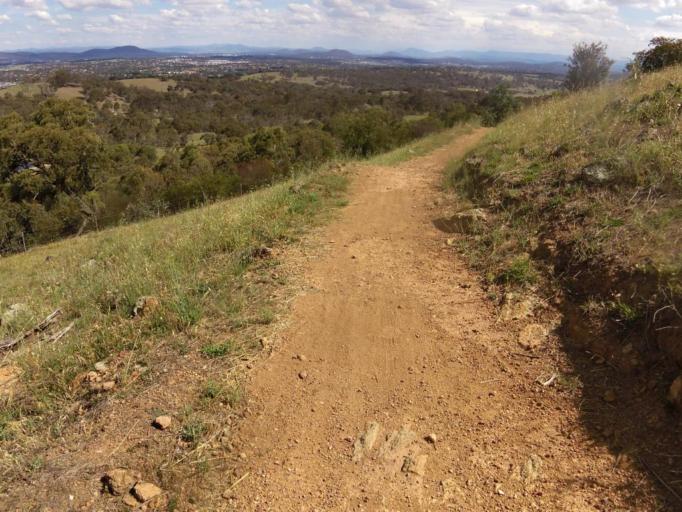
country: AU
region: Australian Capital Territory
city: Belconnen
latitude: -35.1493
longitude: 149.0890
